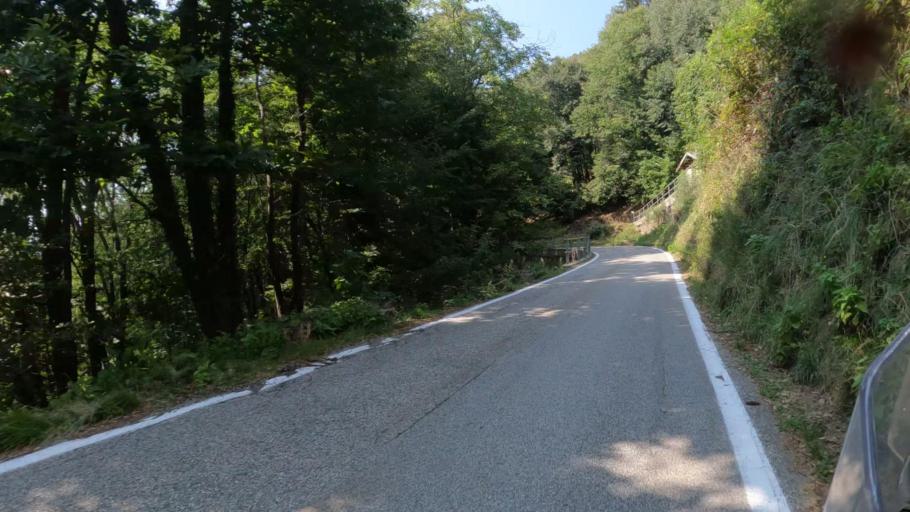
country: IT
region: Lombardy
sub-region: Provincia di Varese
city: Veddasca
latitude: 46.0610
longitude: 8.7774
